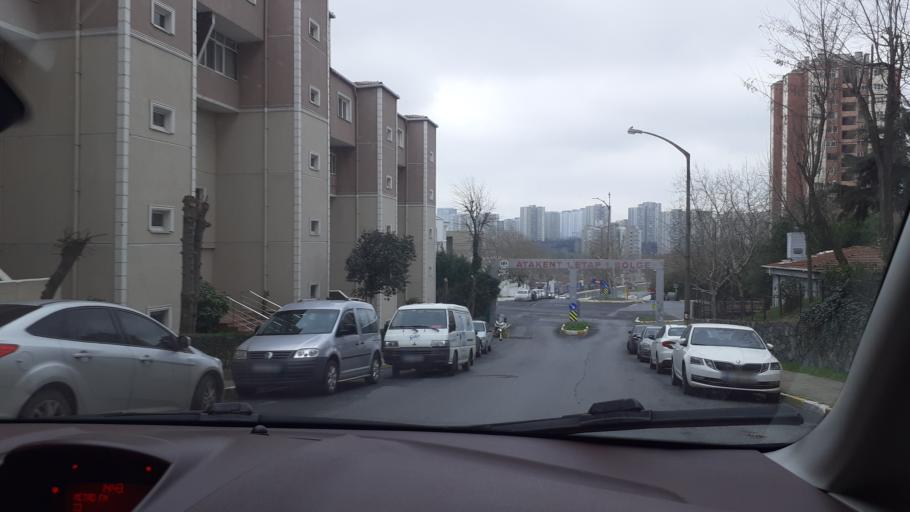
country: TR
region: Istanbul
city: Mahmutbey
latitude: 41.0470
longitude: 28.7907
